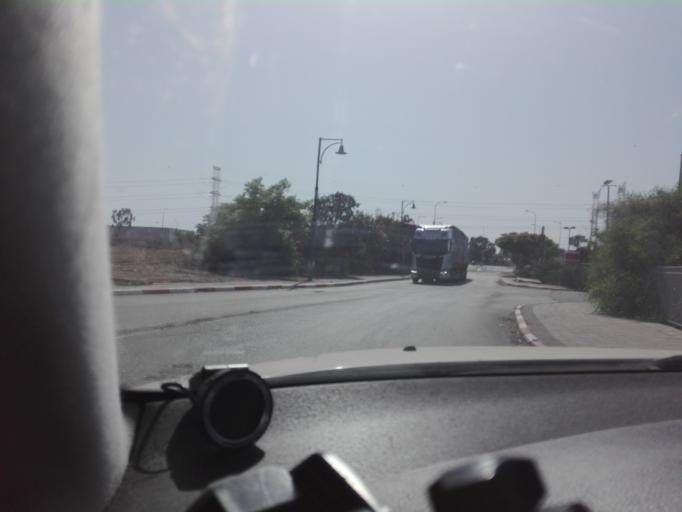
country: IL
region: Central District
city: Bene 'Ayish
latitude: 31.7186
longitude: 34.7560
